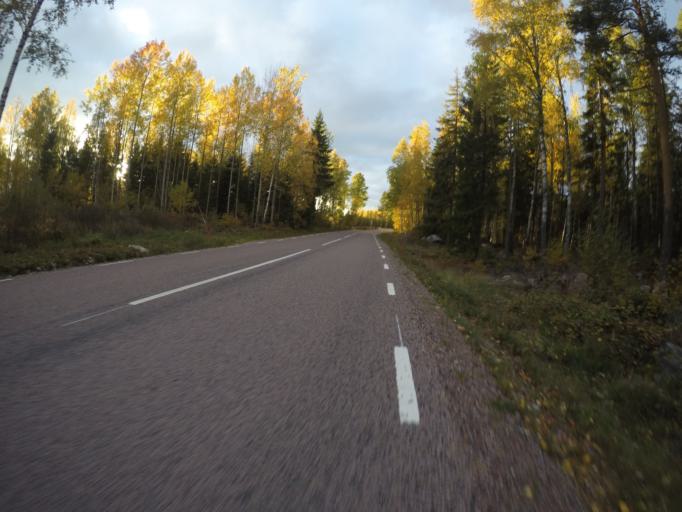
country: SE
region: Vaestmanland
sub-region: Arboga Kommun
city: Tyringe
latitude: 59.3073
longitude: 15.9992
